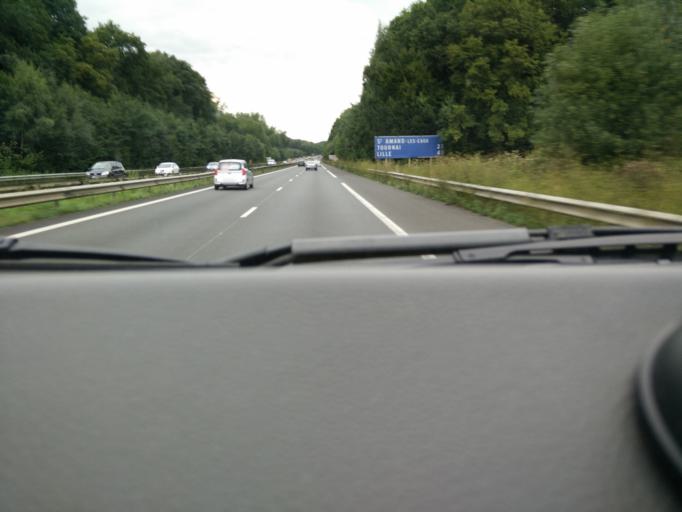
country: FR
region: Nord-Pas-de-Calais
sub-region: Departement du Nord
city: Aubry-du-Hainaut
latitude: 50.3822
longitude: 3.4646
